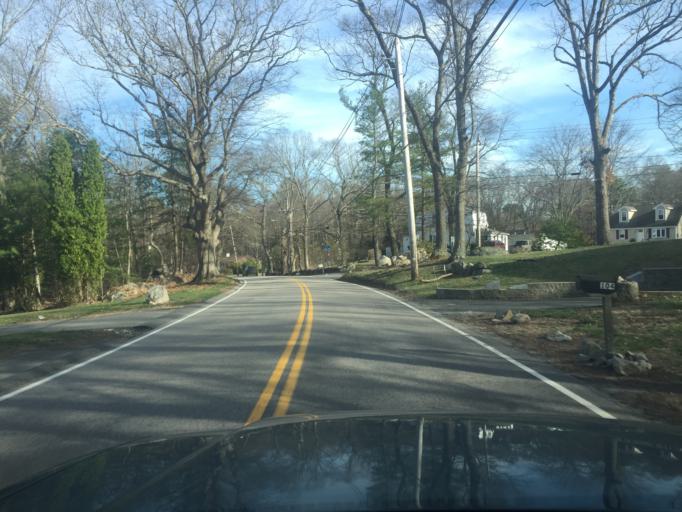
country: US
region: Massachusetts
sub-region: Worcester County
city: Milford
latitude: 42.1432
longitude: -71.4672
